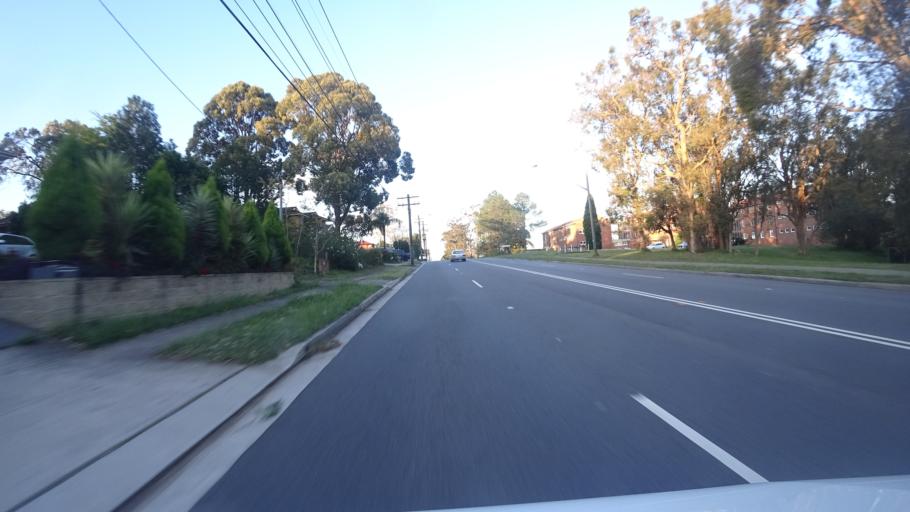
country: AU
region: New South Wales
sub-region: Ryde
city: North Ryde
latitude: -33.7989
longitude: 151.1222
